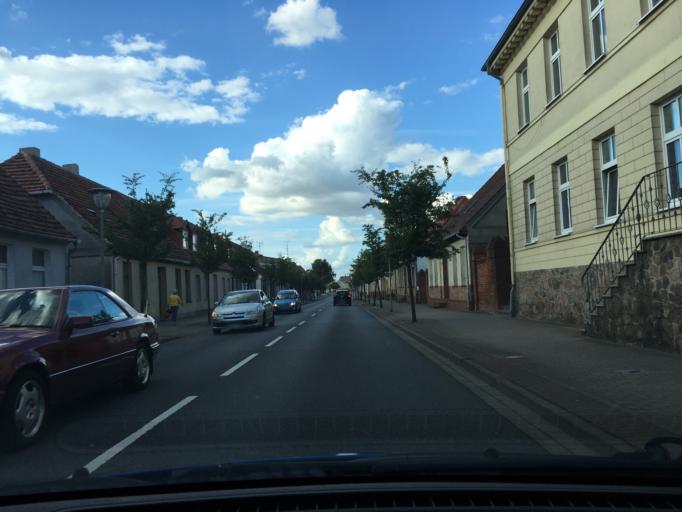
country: DE
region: Mecklenburg-Vorpommern
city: Ludwigslust
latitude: 53.3218
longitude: 11.5000
